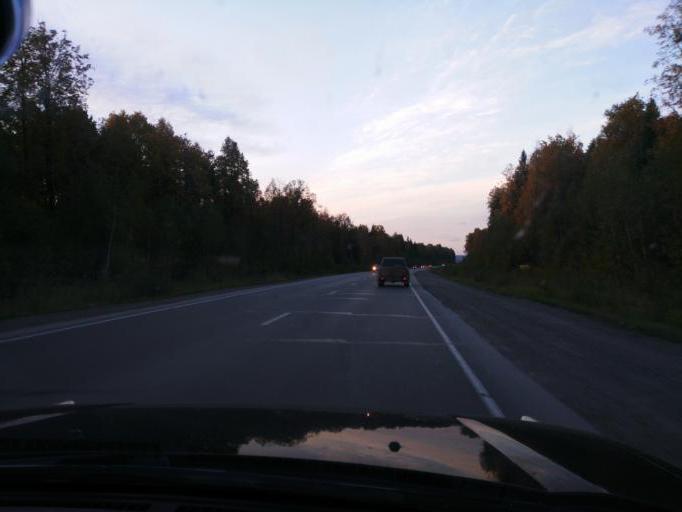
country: RU
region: Perm
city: Polazna
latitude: 58.1277
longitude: 56.4221
